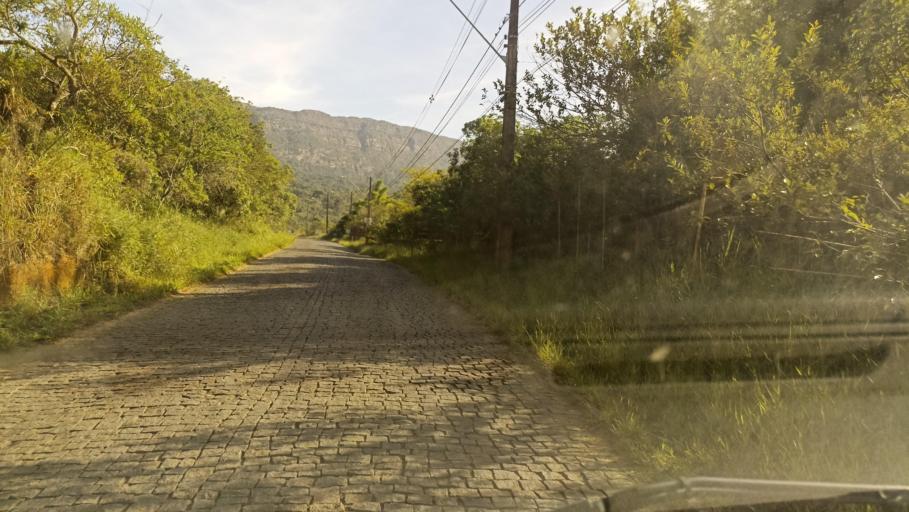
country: BR
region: Minas Gerais
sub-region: Tiradentes
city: Tiradentes
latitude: -21.1180
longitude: -44.1896
